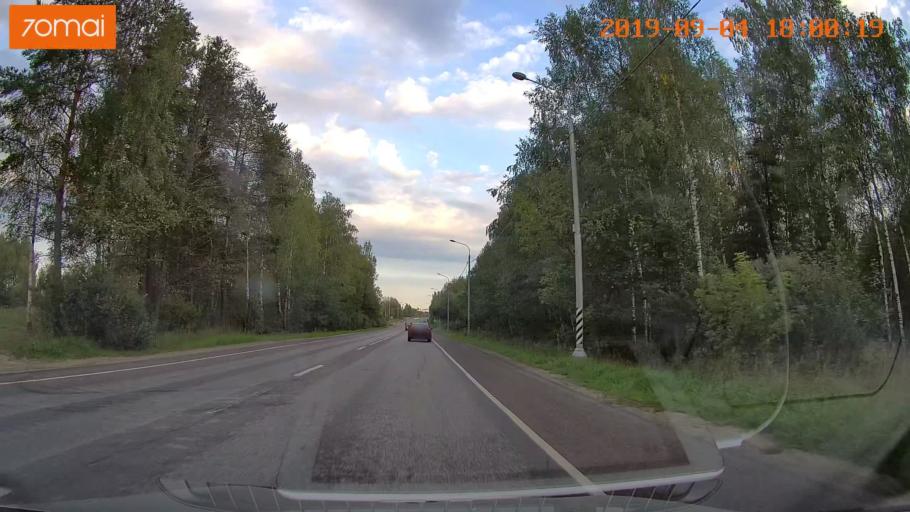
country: RU
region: Moskovskaya
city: Il'inskiy Pogost
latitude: 55.4912
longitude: 38.8596
